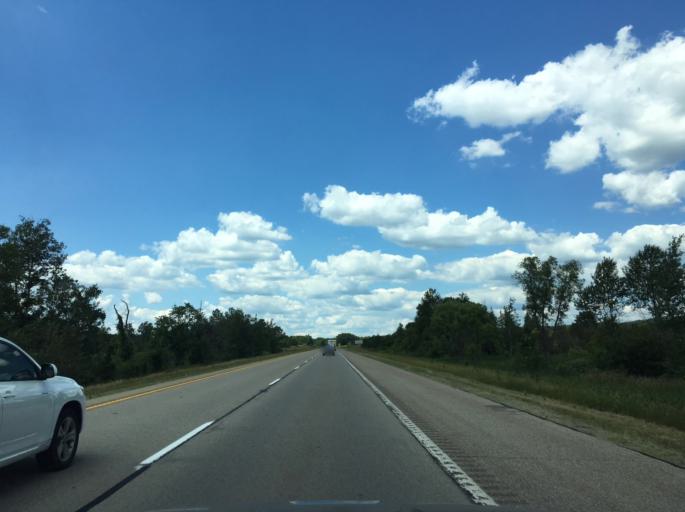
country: US
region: Michigan
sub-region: Clare County
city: Clare
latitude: 43.8820
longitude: -84.7905
